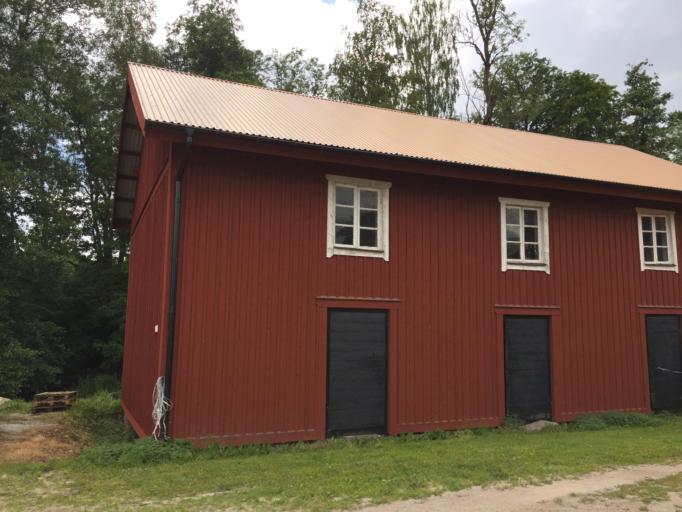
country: SE
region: Vaestmanland
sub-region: Norbergs Kommun
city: Norberg
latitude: 60.0304
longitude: 15.9623
